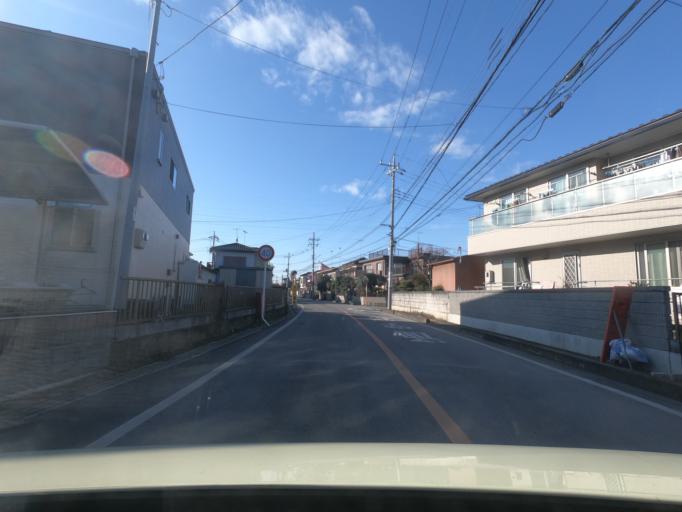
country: JP
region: Ibaraki
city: Koga
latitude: 36.2374
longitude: 139.7539
